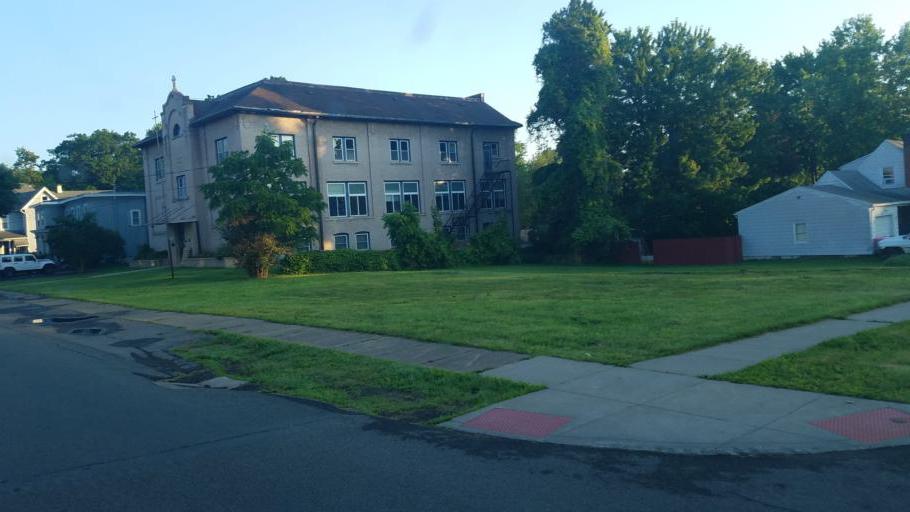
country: US
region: New York
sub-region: Wayne County
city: Clyde
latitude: 43.0867
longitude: -76.8699
